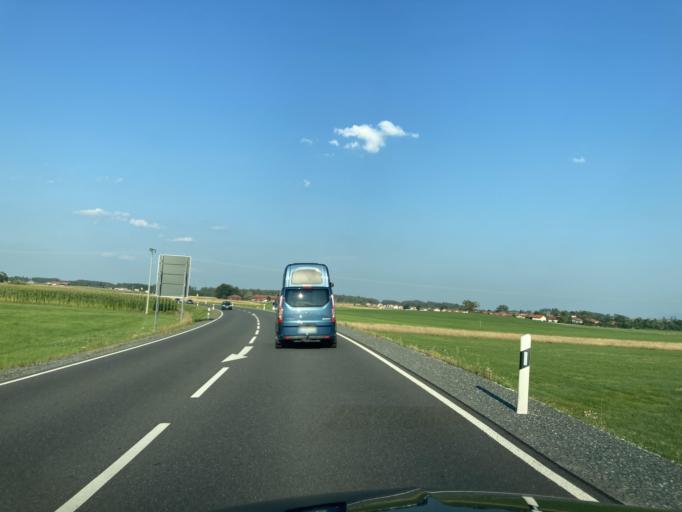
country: DE
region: Bavaria
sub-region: Upper Bavaria
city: Obing
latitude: 48.0106
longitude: 12.3947
